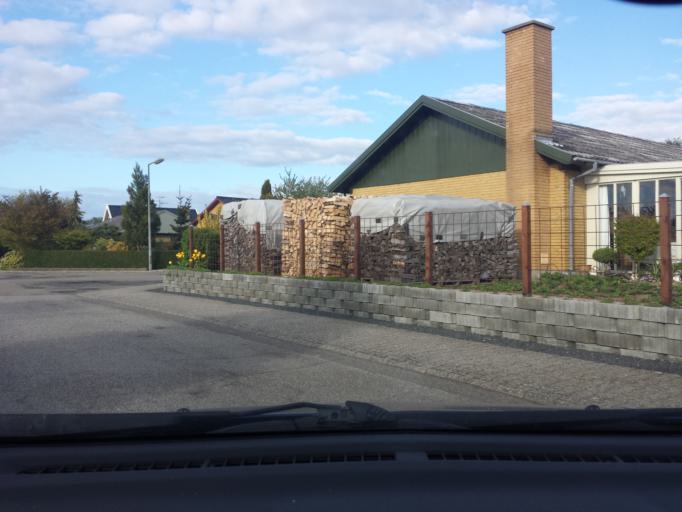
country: DK
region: South Denmark
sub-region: Langeland Kommune
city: Rudkobing
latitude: 54.8595
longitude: 10.7275
